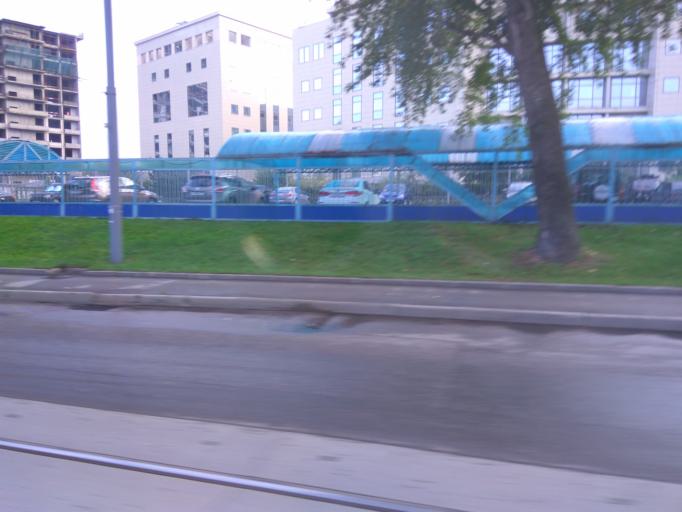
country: RU
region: Moskovskaya
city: Bogorodskoye
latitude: 55.8024
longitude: 37.7096
